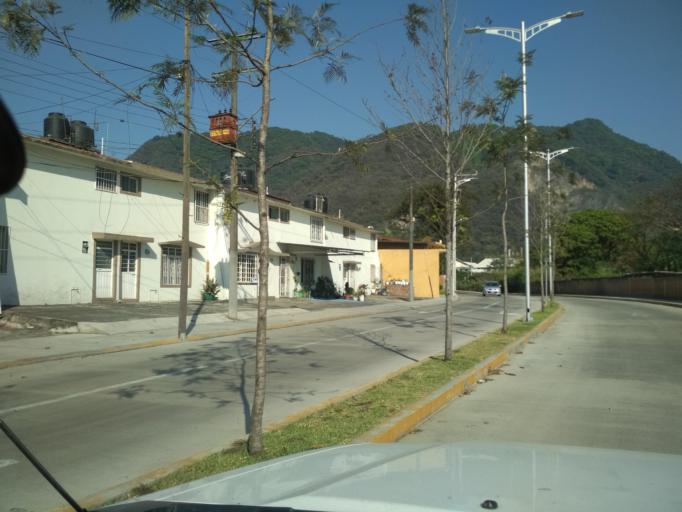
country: MX
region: Veracruz
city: Ixtac Zoquitlan
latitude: 18.8599
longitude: -97.0708
